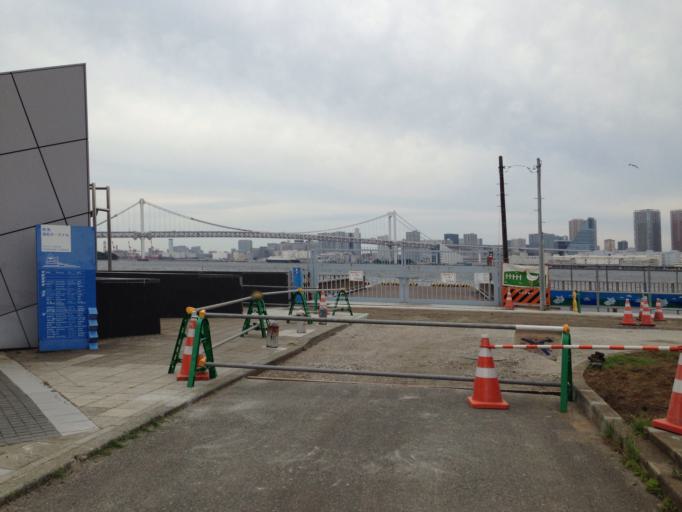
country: JP
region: Tokyo
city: Tokyo
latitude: 35.6470
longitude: 139.7721
